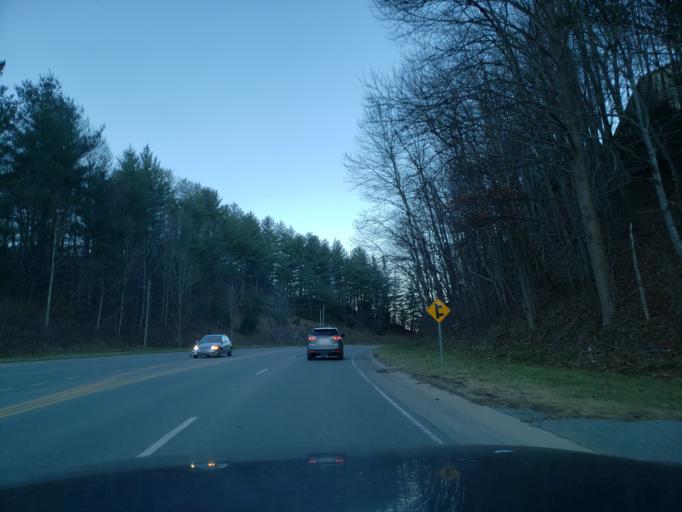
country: US
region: North Carolina
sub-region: Watauga County
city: Boone
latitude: 36.1817
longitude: -81.6493
